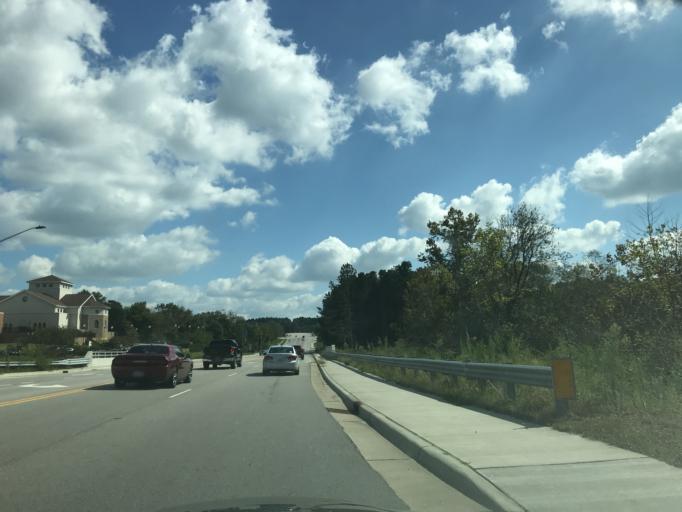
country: US
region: North Carolina
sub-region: Wake County
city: Wake Forest
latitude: 35.9497
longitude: -78.5092
